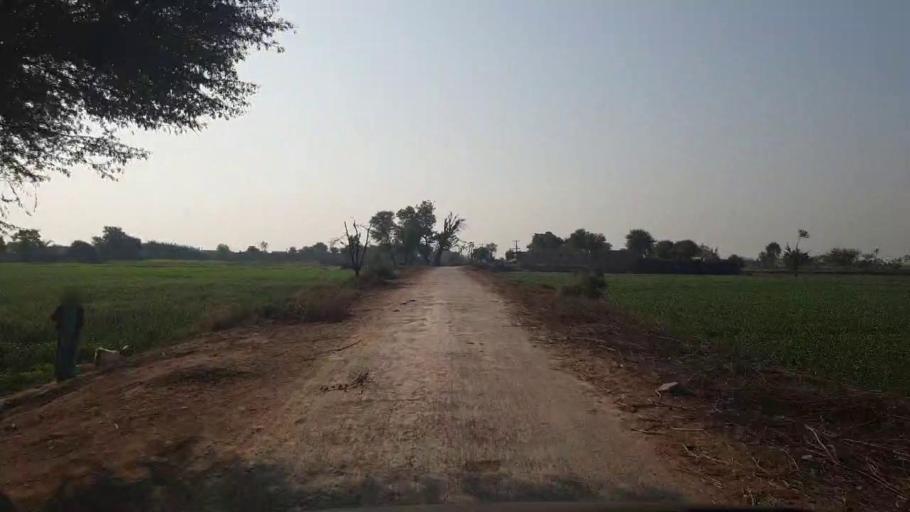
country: PK
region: Sindh
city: Tando Adam
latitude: 25.7504
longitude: 68.6047
